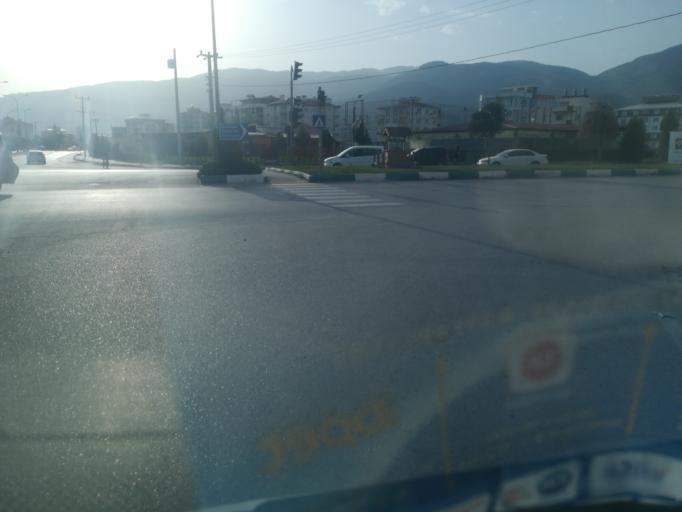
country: TR
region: Osmaniye
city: Osmaniye
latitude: 37.0502
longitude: 36.2280
